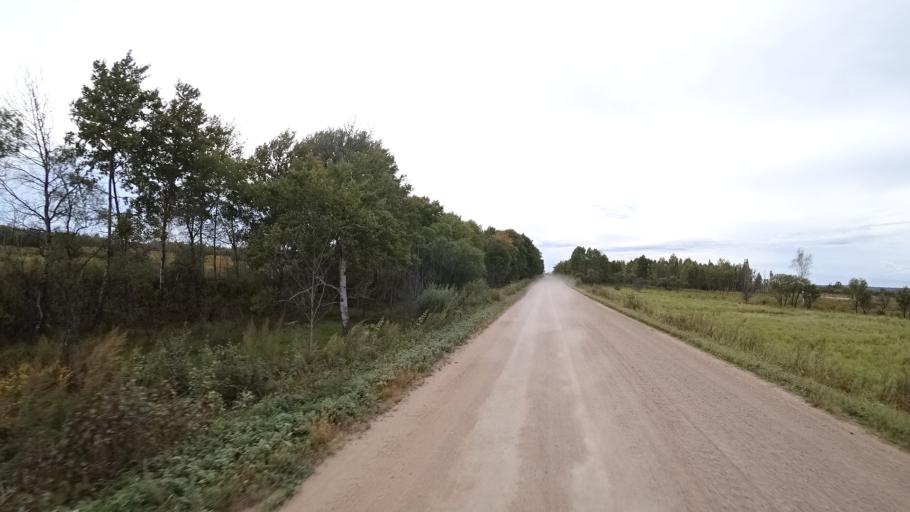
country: RU
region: Amur
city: Arkhara
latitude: 49.3750
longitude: 130.1955
